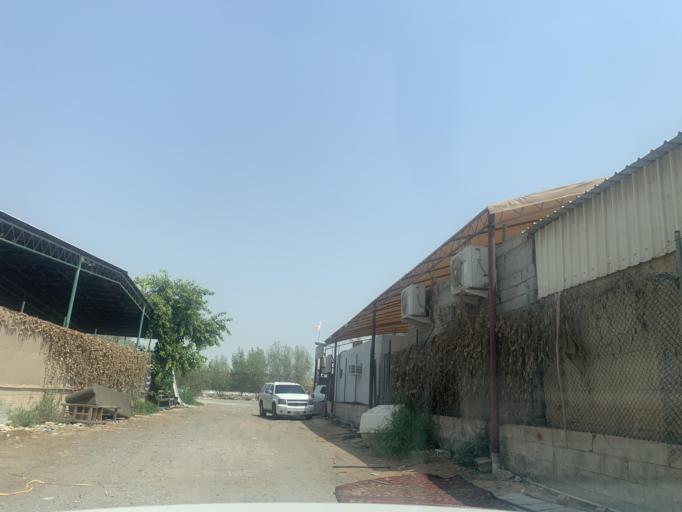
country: BH
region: Central Governorate
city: Madinat Hamad
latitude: 26.1427
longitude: 50.4784
